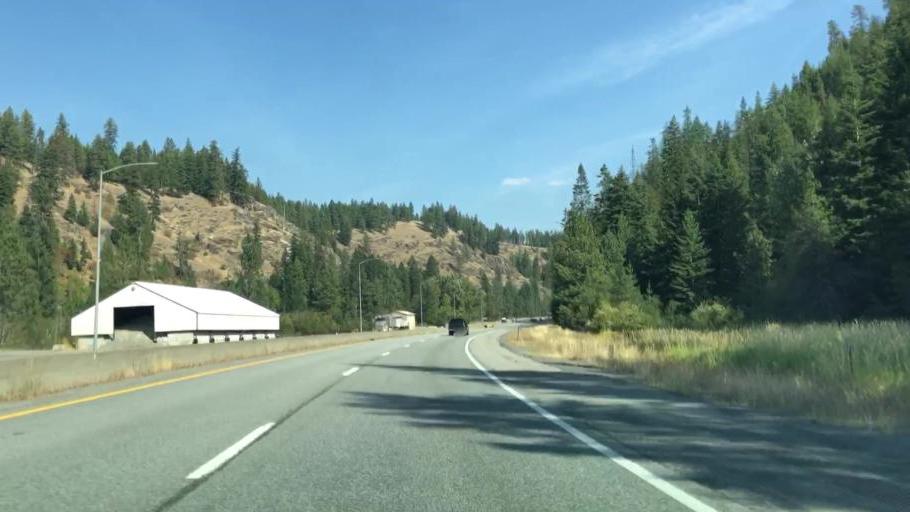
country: US
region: Idaho
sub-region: Kootenai County
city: Coeur d'Alene
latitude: 47.6306
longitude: -116.6113
